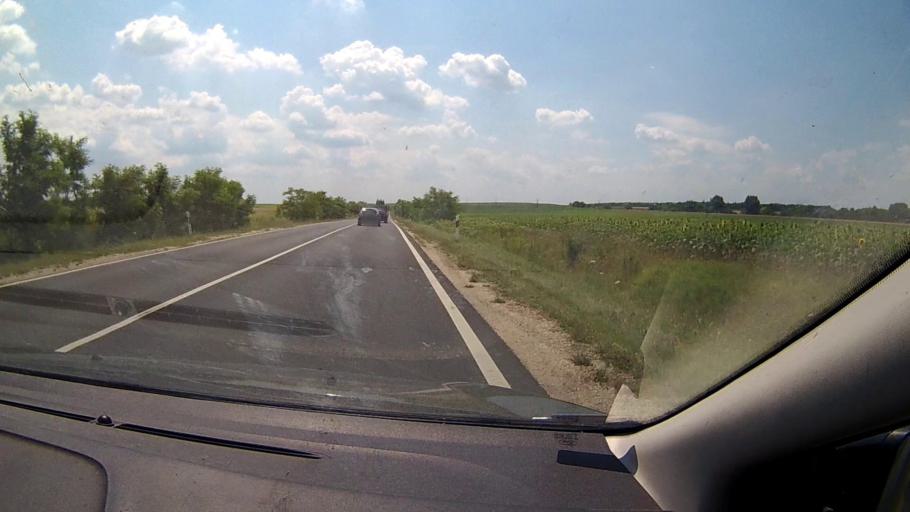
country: HU
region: Komarom-Esztergom
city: Tata
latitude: 47.6062
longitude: 18.3178
